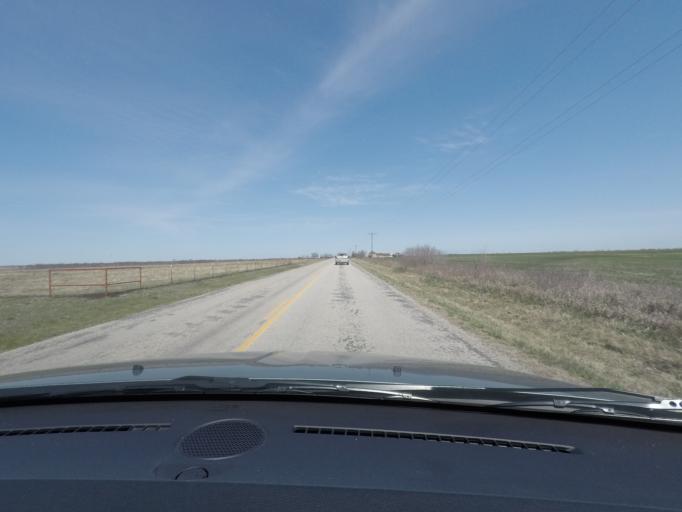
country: US
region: Kansas
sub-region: Lyon County
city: Emporia
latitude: 38.5144
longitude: -96.1704
